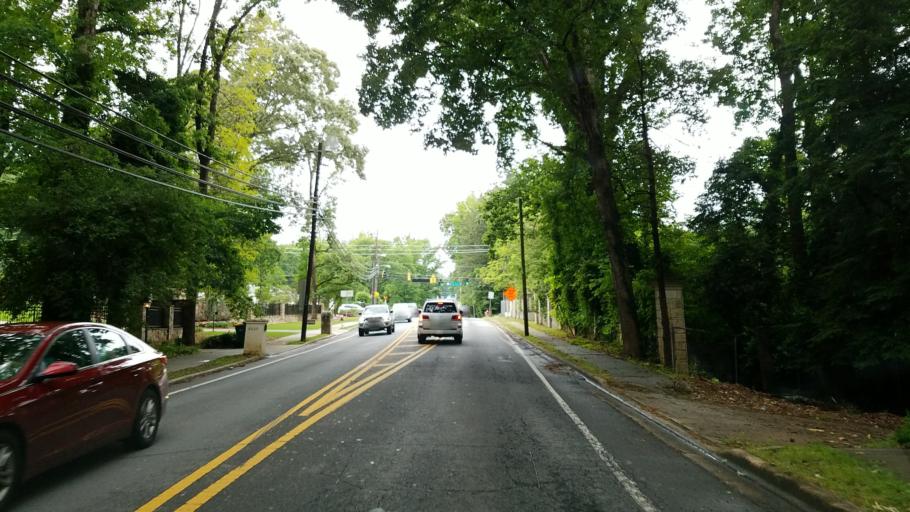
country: US
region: Georgia
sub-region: Fulton County
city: Sandy Springs
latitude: 33.9203
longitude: -84.4066
